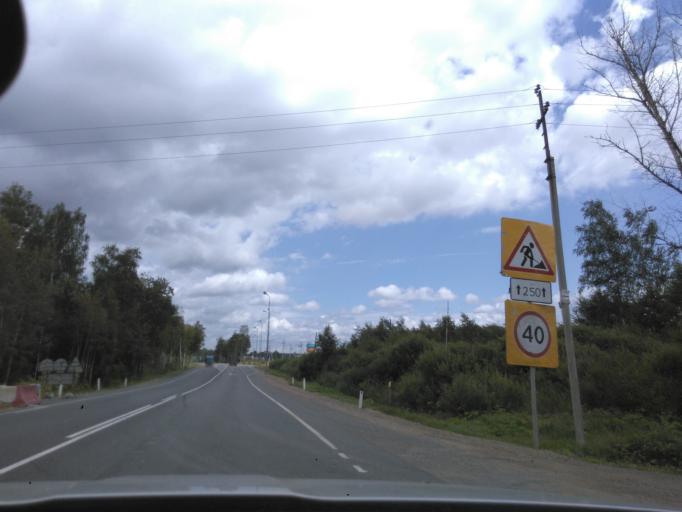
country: RU
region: Moskovskaya
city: Radumlya
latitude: 56.0532
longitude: 37.1302
